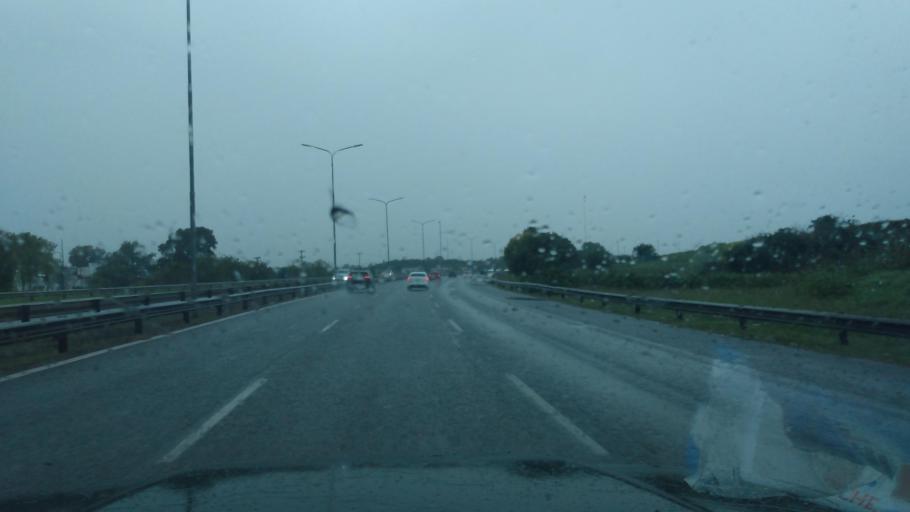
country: AR
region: Buenos Aires
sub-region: Partido de Tigre
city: Tigre
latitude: -34.4994
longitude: -58.5919
